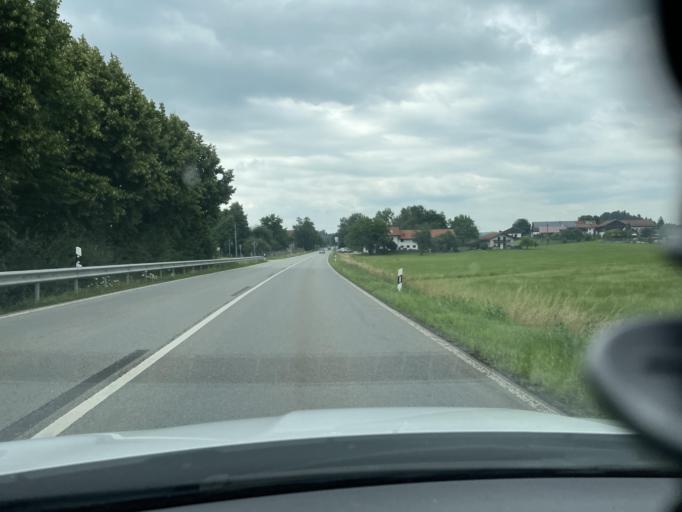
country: DE
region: Bavaria
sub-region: Upper Bavaria
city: Soyen
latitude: 48.0930
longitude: 12.1958
